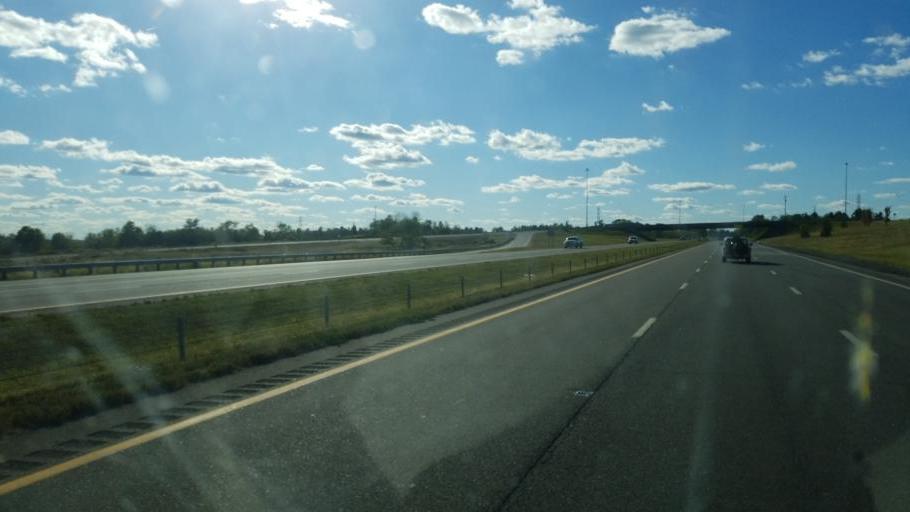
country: US
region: Ohio
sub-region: Belmont County
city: Wolfhurst
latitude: 40.0493
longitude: -80.7911
